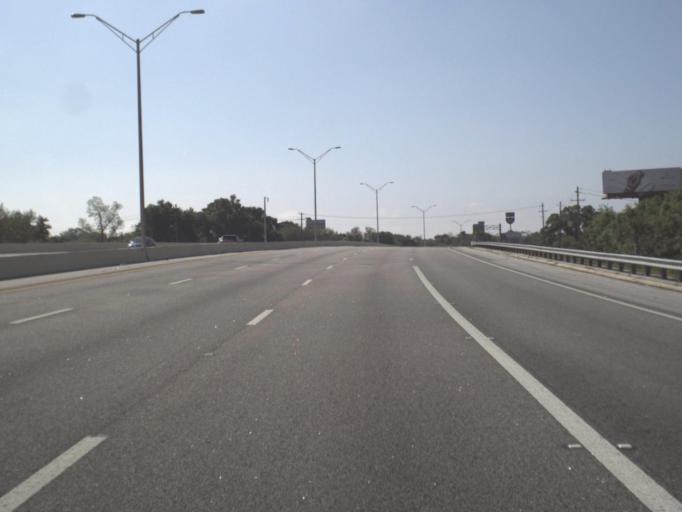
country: US
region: Florida
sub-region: Escambia County
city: Goulding
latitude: 30.4482
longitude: -87.2189
